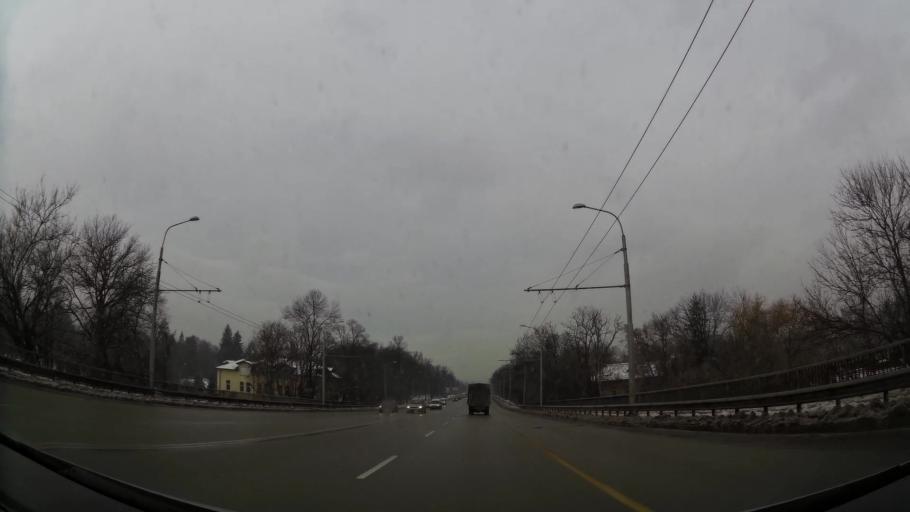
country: BG
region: Sofia-Capital
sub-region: Stolichna Obshtina
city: Sofia
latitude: 42.7132
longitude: 23.2874
